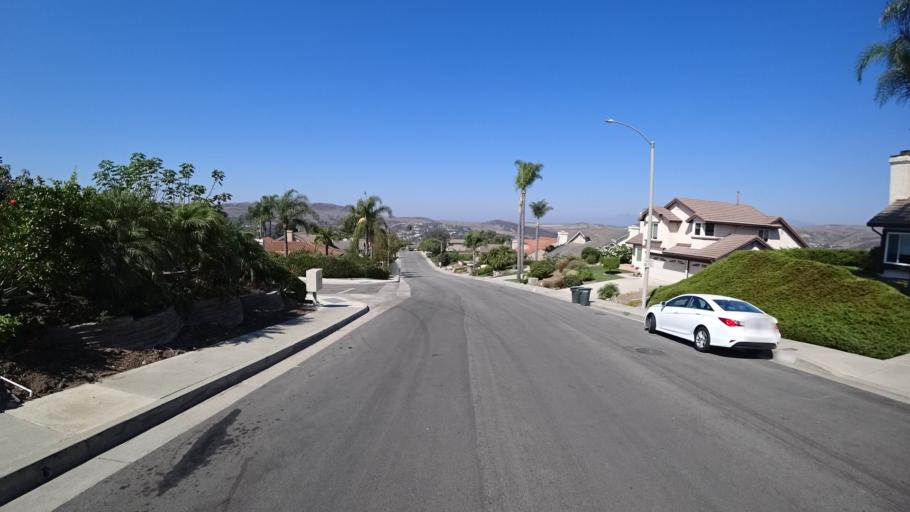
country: US
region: California
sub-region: Orange County
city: San Clemente
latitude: 33.4606
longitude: -117.6279
